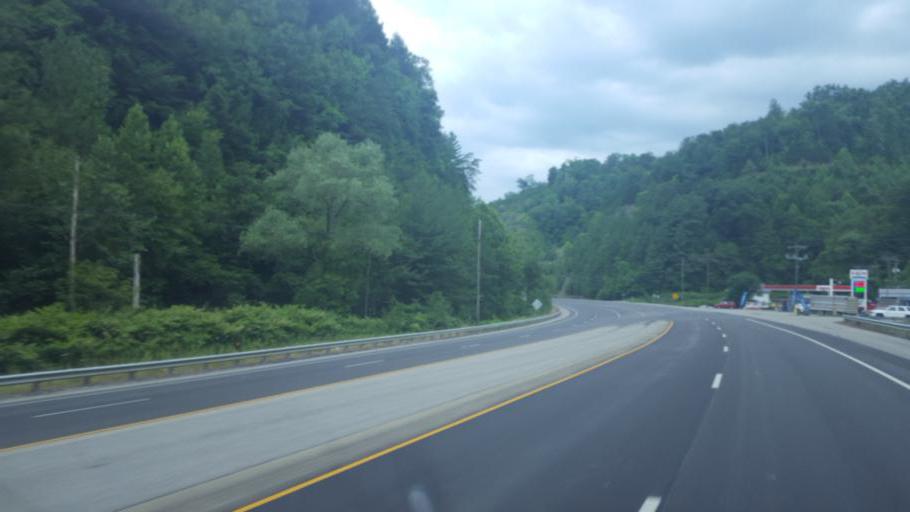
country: US
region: Kentucky
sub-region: Letcher County
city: Jenkins
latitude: 37.2822
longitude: -82.5712
